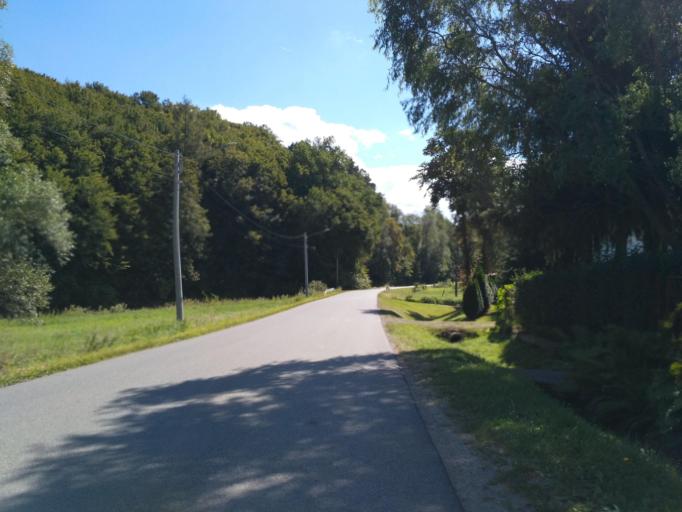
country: PL
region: Subcarpathian Voivodeship
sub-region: Powiat jasielski
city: Skolyszyn
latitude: 49.7953
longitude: 21.3252
